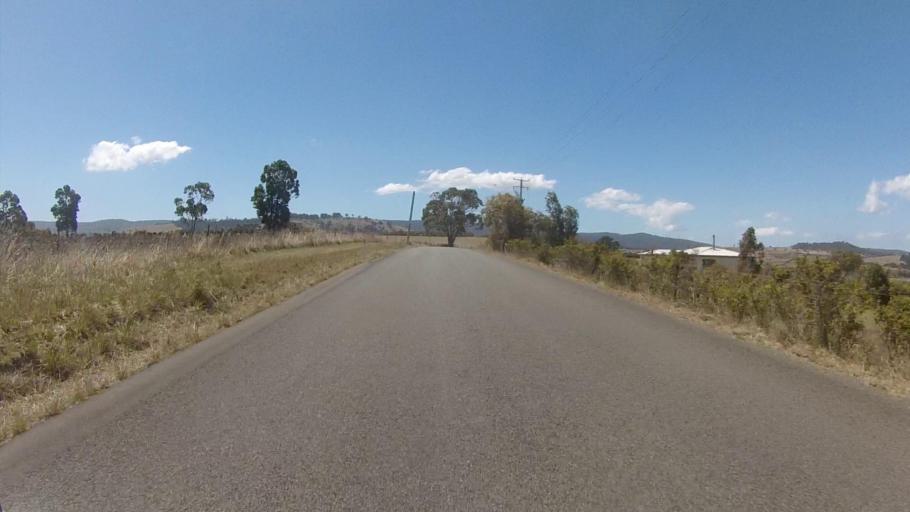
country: AU
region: Tasmania
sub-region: Sorell
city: Sorell
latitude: -42.7743
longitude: 147.5814
